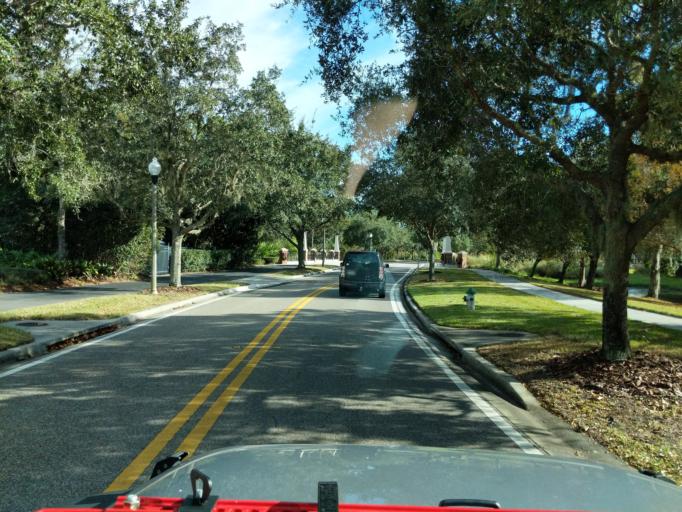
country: US
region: Florida
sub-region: Orange County
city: Lake Butler
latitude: 28.4680
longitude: -81.5983
